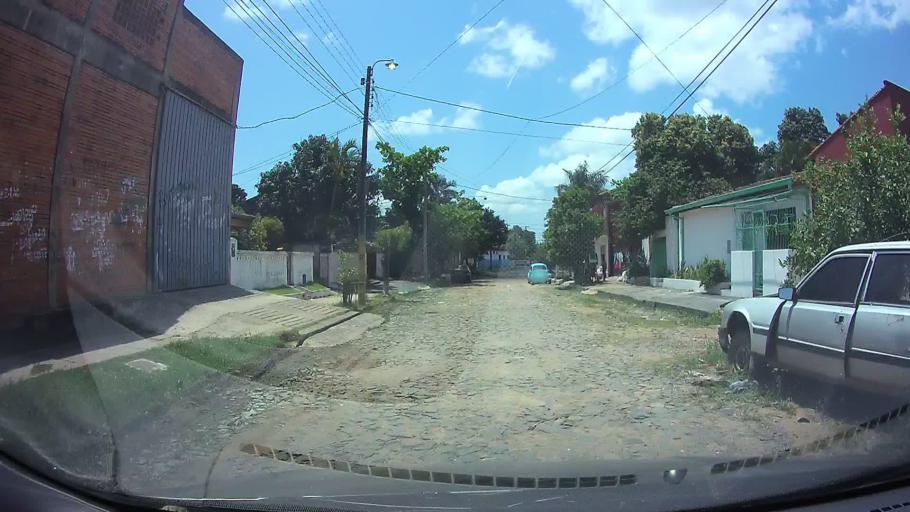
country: PY
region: Central
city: Fernando de la Mora
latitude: -25.3007
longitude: -57.5499
